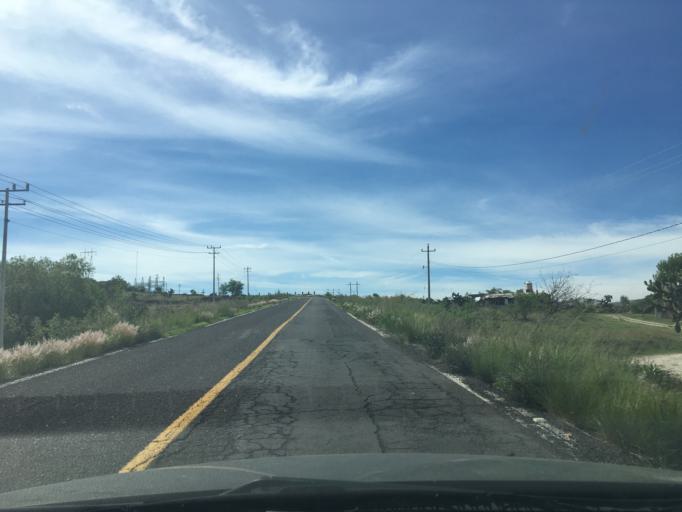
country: MX
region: Guanajuato
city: Coroneo
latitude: 20.1903
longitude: -100.3588
